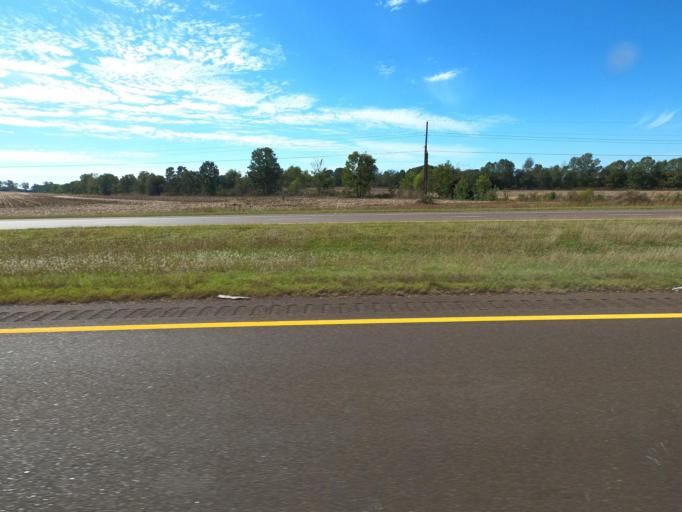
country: US
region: Tennessee
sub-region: Lauderdale County
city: Halls
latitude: 35.9208
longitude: -89.2762
